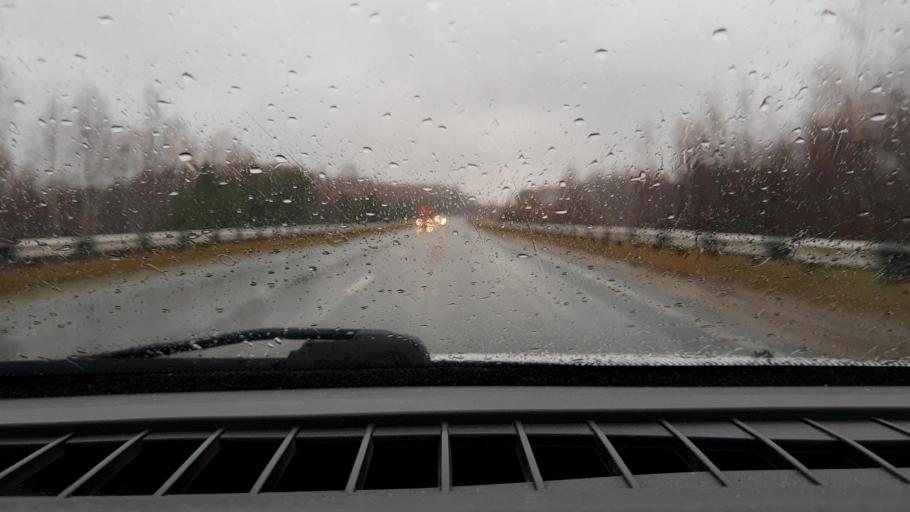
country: RU
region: Nizjnij Novgorod
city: Sitniki
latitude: 56.4788
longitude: 44.0257
